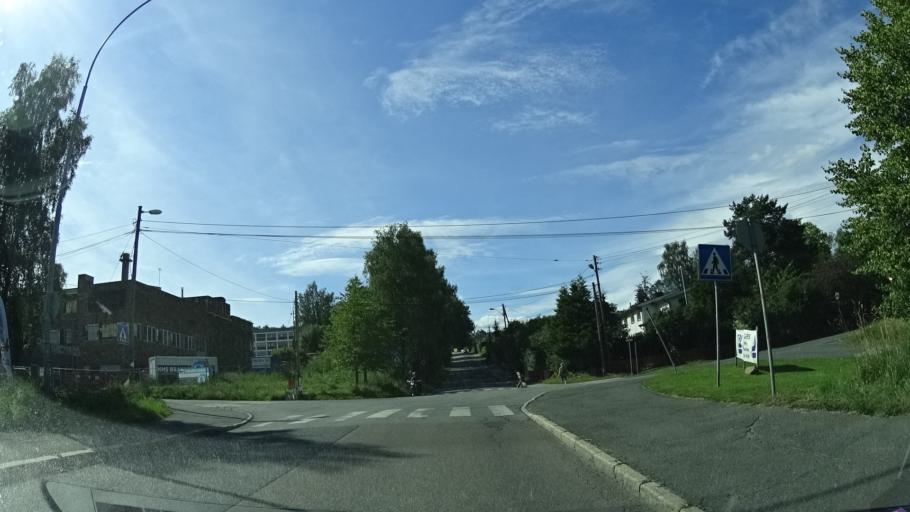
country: NO
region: Oslo
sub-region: Oslo
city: Oslo
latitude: 59.9668
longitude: 10.7740
